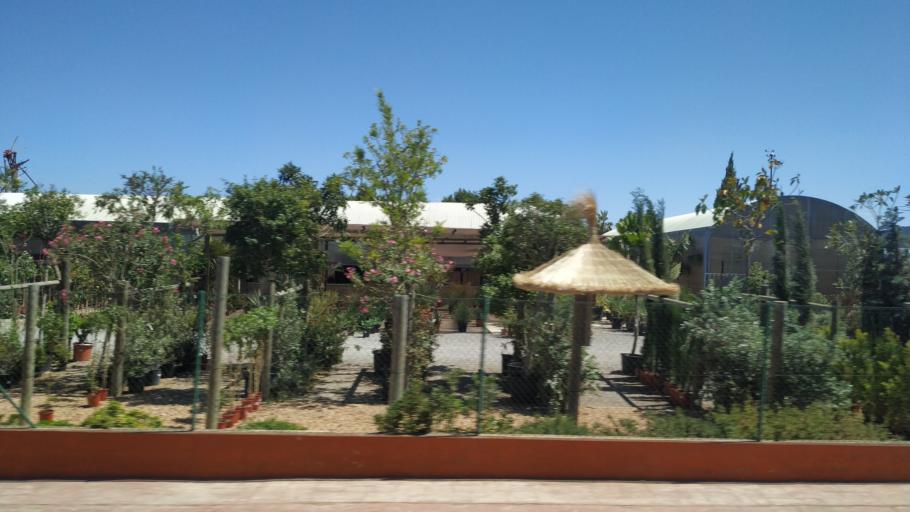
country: ES
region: Balearic Islands
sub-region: Illes Balears
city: Ibiza
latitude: 38.8819
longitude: 1.3764
